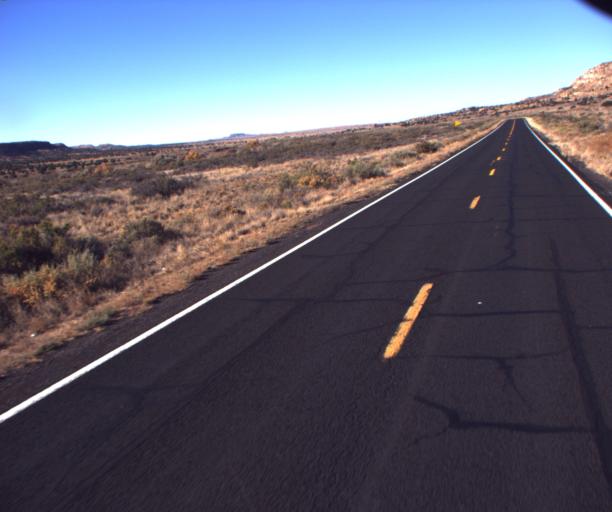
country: US
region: Arizona
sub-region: Navajo County
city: First Mesa
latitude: 35.8412
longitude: -110.2500
